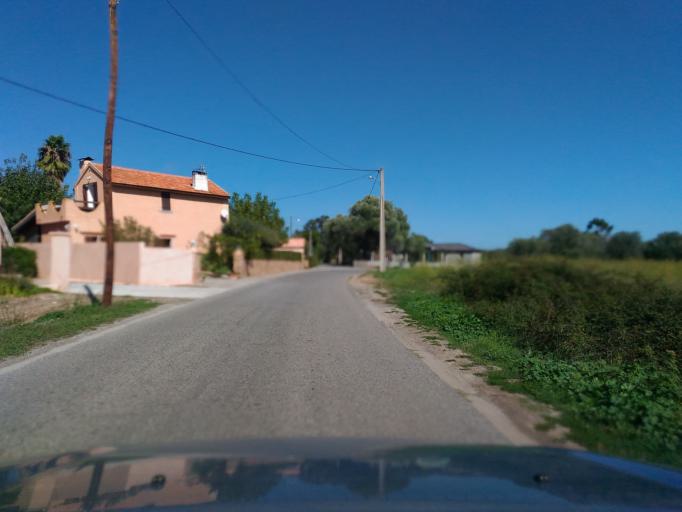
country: FR
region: Corsica
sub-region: Departement de la Haute-Corse
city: Aleria
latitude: 42.1142
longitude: 9.4815
